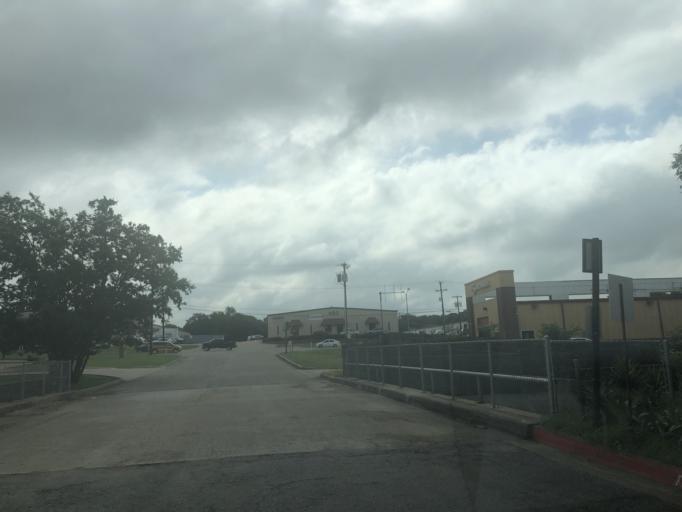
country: US
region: Texas
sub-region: Dallas County
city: Irving
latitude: 32.8109
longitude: -96.9950
